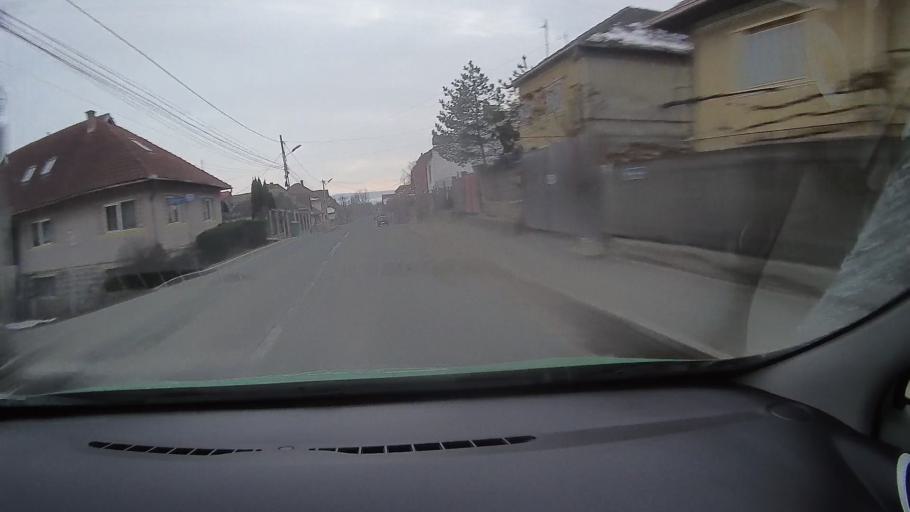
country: RO
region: Harghita
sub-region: Municipiul Odorheiu Secuiesc
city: Odorheiu Secuiesc
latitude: 46.3084
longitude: 25.2859
